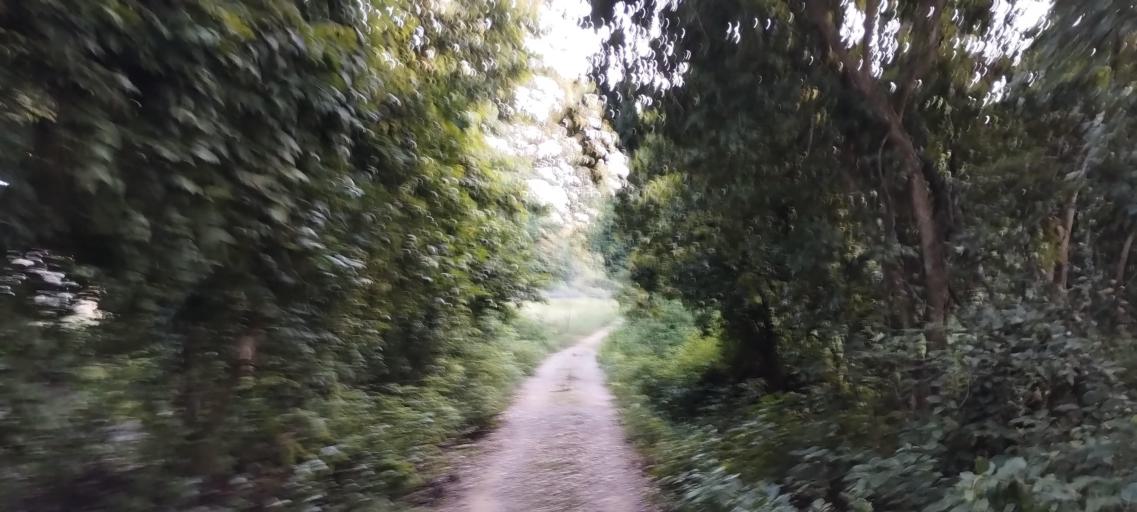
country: NP
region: Far Western
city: Tikapur
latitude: 28.4552
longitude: 81.2422
